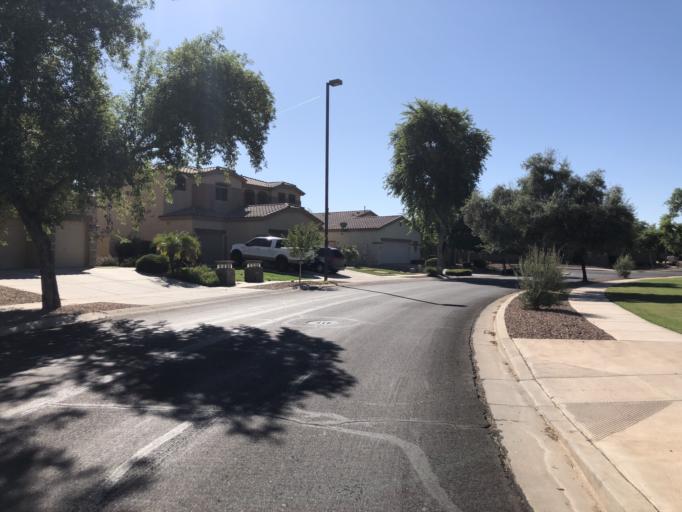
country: US
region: Arizona
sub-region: Maricopa County
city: Queen Creek
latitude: 33.2667
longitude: -111.6989
